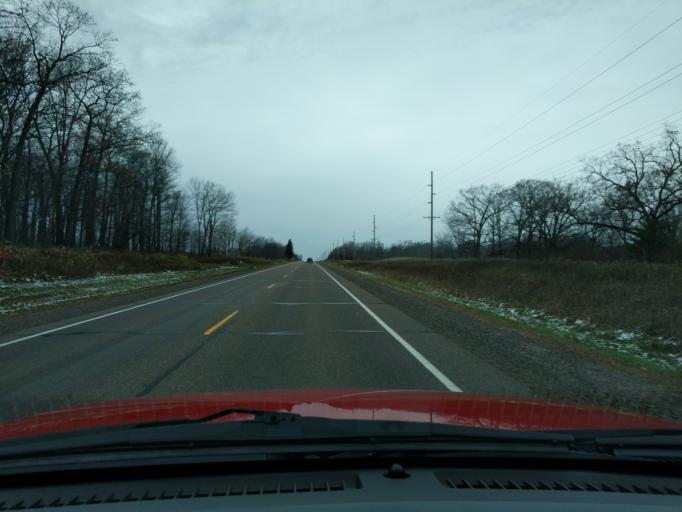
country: US
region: Wisconsin
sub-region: Washburn County
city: Shell Lake
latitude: 45.8153
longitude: -92.0260
